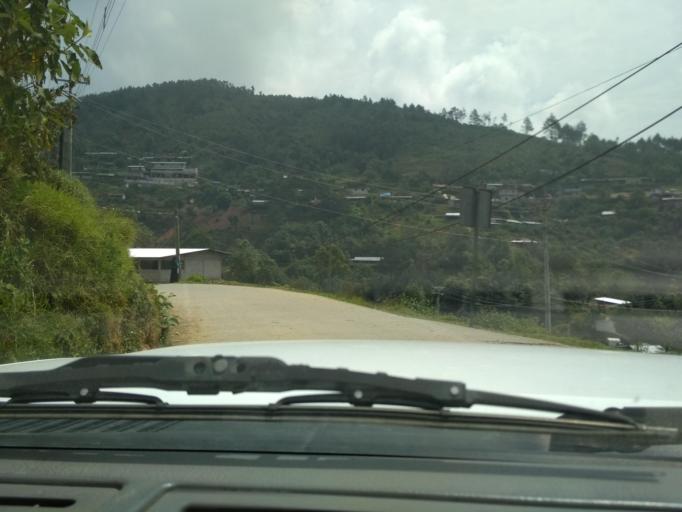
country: MX
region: Veracruz
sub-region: Camerino Z. Mendoza
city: Necoxtla
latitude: 18.7807
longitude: -97.1538
